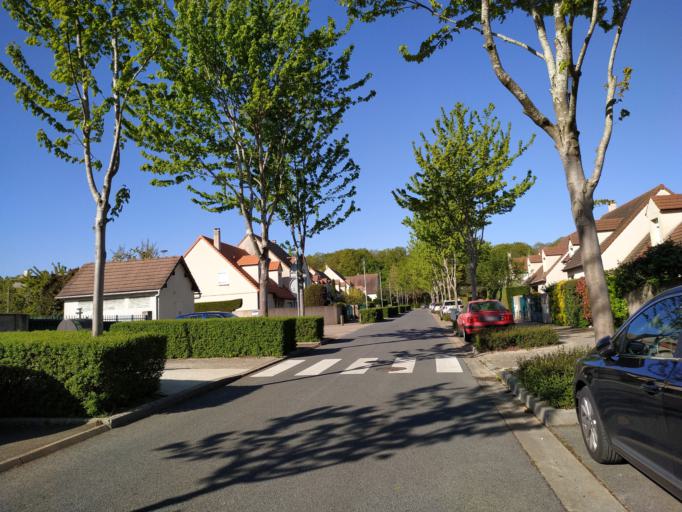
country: FR
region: Ile-de-France
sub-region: Departement des Yvelines
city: Bois-d'Arcy
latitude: 48.8051
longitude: 2.0198
